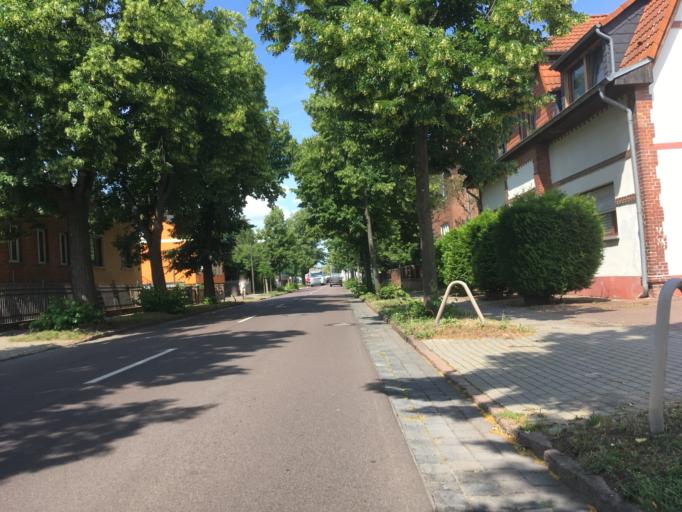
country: DE
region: Saxony-Anhalt
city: Koethen
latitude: 51.7538
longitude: 12.0050
